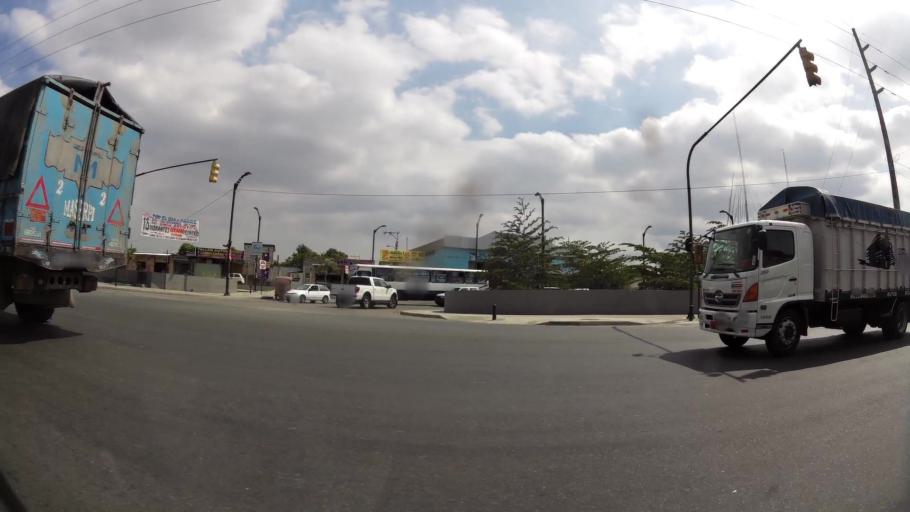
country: EC
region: Guayas
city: Eloy Alfaro
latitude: -2.0686
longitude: -79.9245
